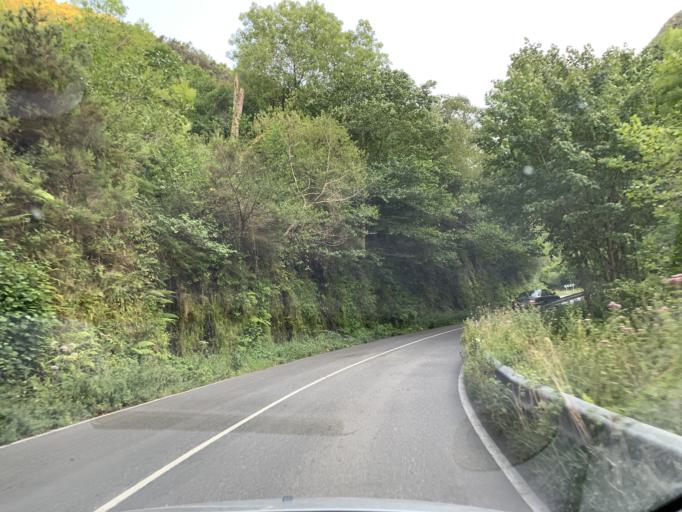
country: ES
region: Asturias
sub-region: Province of Asturias
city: Carrena
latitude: 43.3530
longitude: -4.9141
